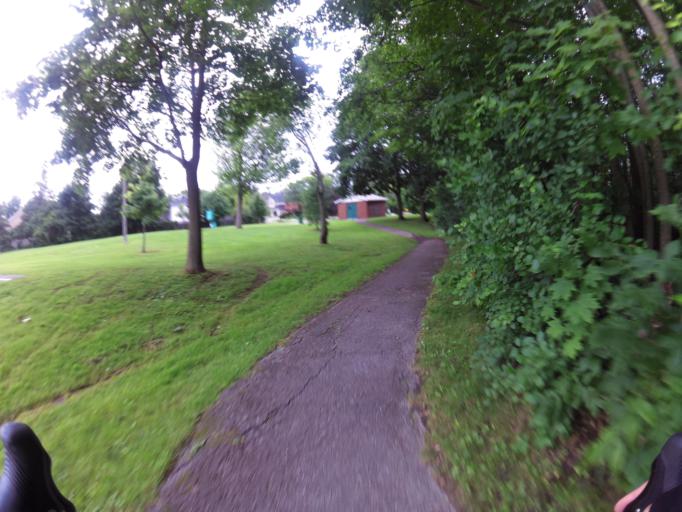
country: CA
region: Ontario
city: Ottawa
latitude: 45.3209
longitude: -75.7081
